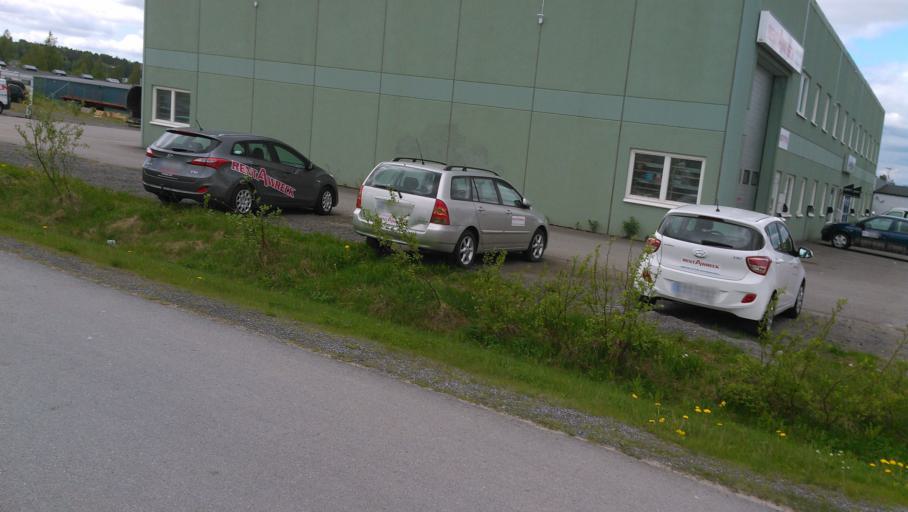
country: SE
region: Vaesterbotten
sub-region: Umea Kommun
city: Ersmark
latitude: 63.8504
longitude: 20.3147
